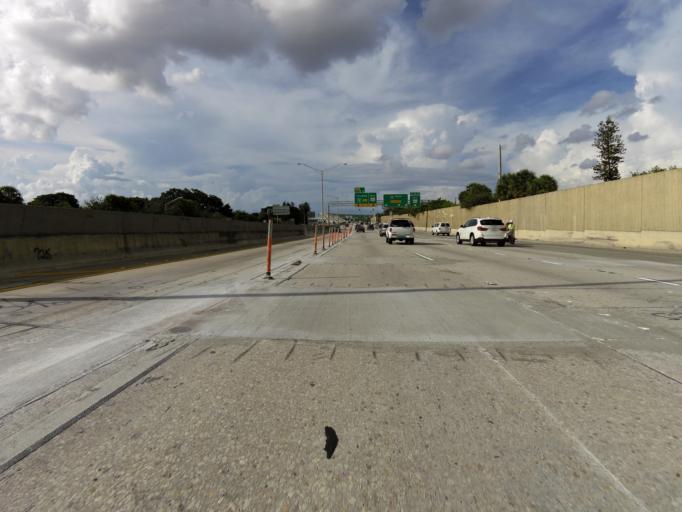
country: US
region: Florida
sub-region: Miami-Dade County
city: Golden Glades
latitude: 25.9143
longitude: -80.2100
